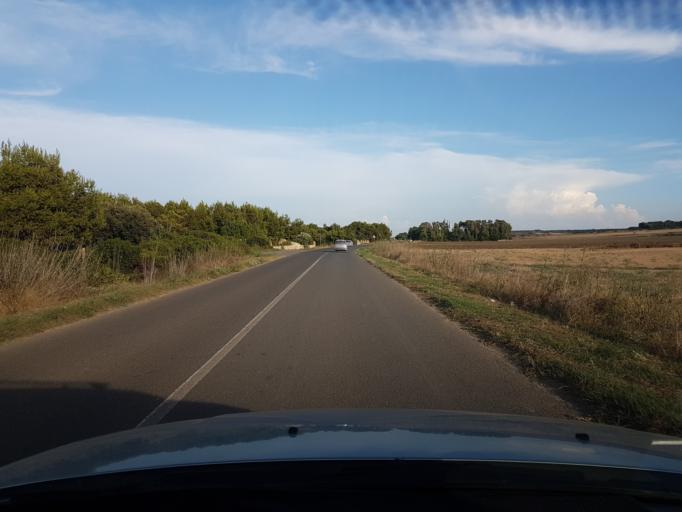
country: IT
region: Sardinia
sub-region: Provincia di Oristano
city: Cabras
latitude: 39.9493
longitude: 8.4282
